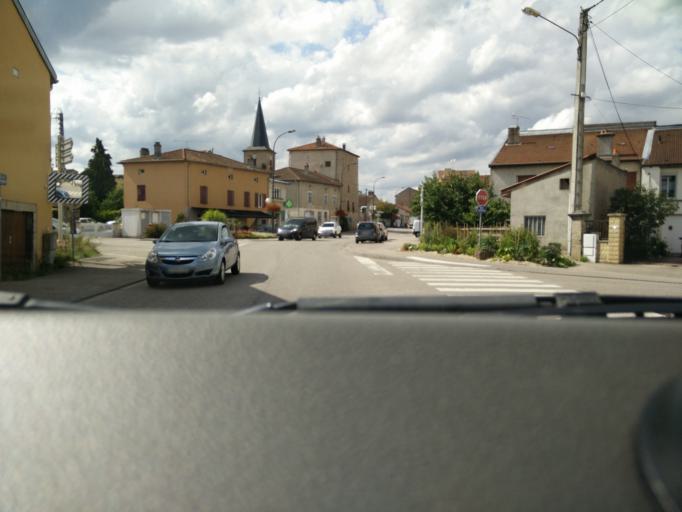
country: FR
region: Lorraine
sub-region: Departement de Meurthe-et-Moselle
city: Damelevieres
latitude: 48.5569
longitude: 6.3890
